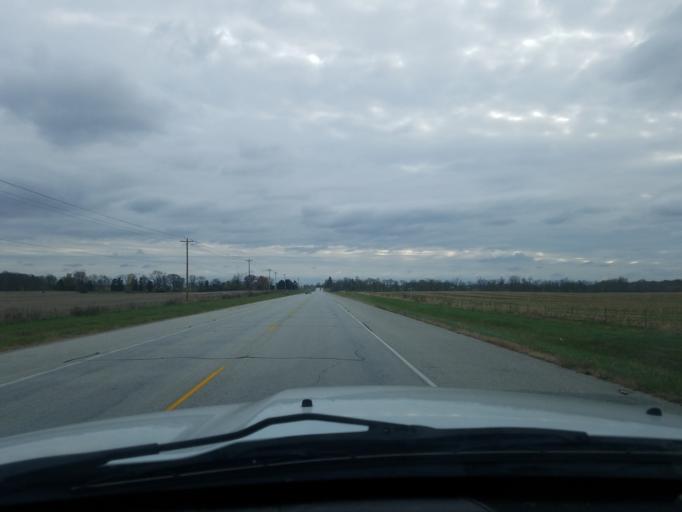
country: US
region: Indiana
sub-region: Bartholomew County
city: Hope
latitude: 39.2028
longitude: -85.7720
